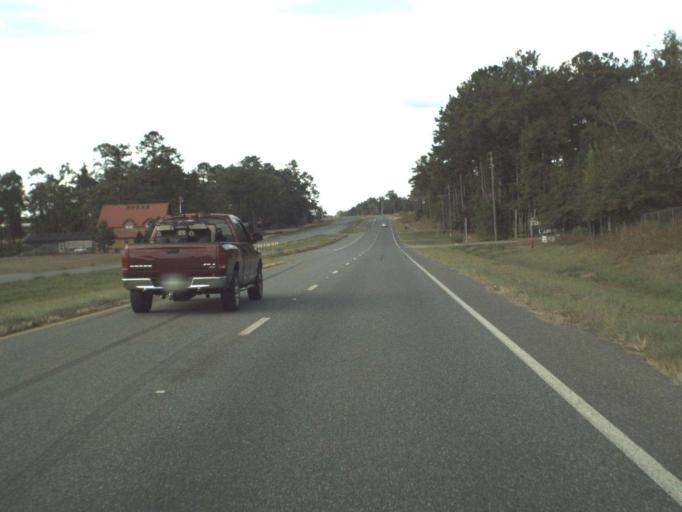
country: US
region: Florida
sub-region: Jefferson County
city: Monticello
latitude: 30.5829
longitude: -83.8700
